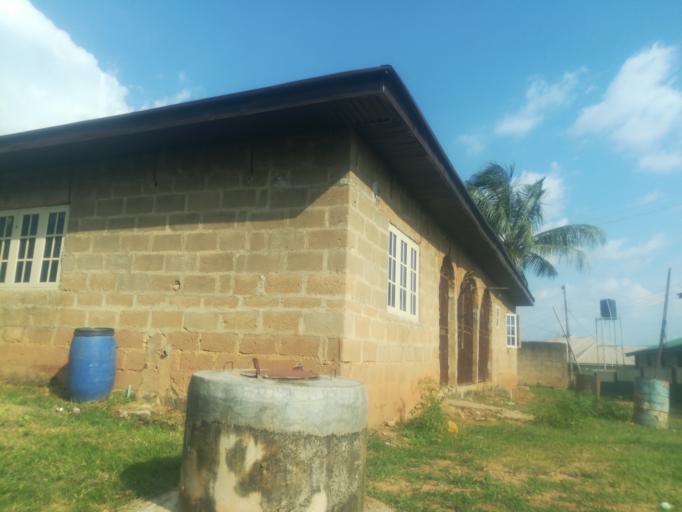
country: NG
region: Oyo
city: Ibadan
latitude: 7.4201
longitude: 3.8424
